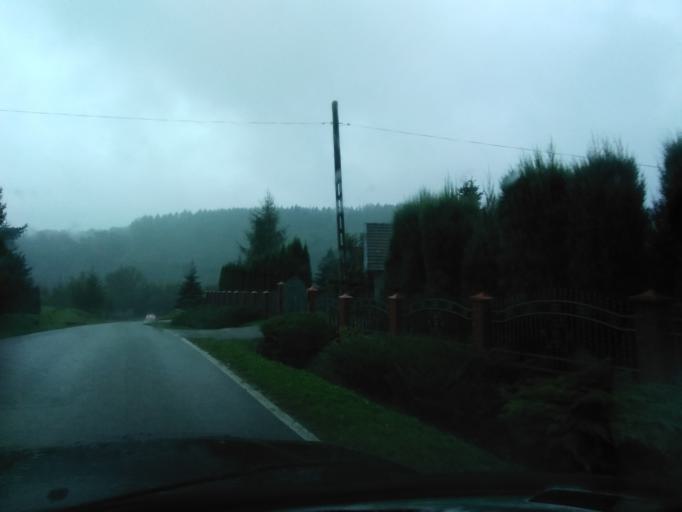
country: PL
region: Subcarpathian Voivodeship
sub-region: Powiat ropczycko-sedziszowski
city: Niedzwiada
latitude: 50.0382
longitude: 21.5445
